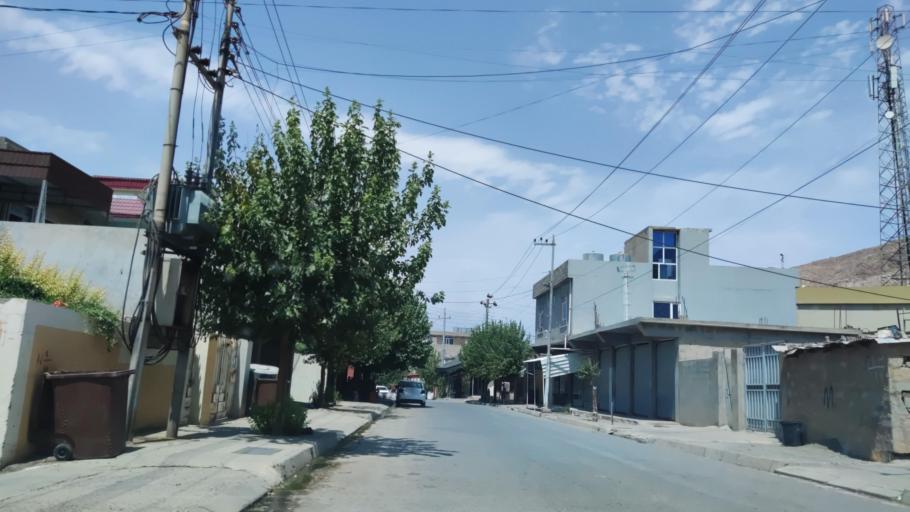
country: IQ
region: Arbil
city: Shaqlawah
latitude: 36.5509
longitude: 44.3562
